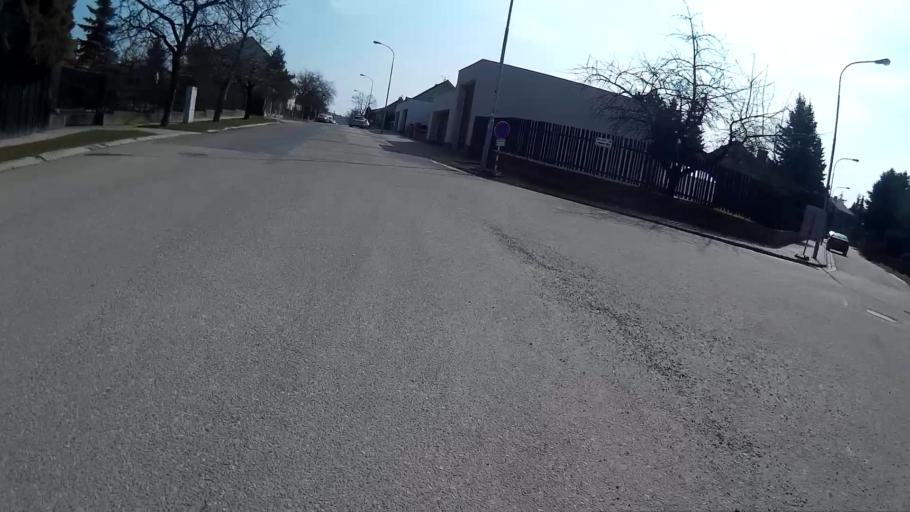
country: CZ
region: South Moravian
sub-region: Mesto Brno
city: Mokra Hora
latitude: 49.2585
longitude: 16.6191
